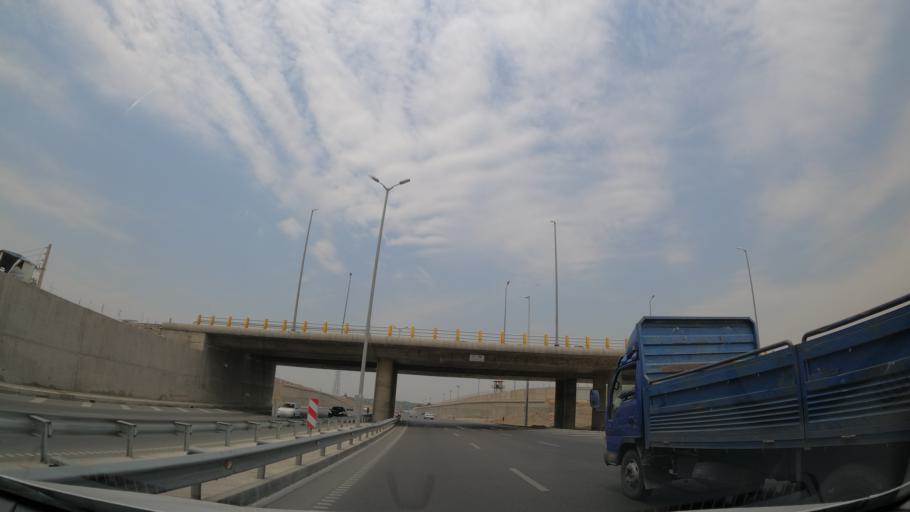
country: IR
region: Tehran
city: Shahr-e Qods
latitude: 35.7415
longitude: 51.2439
